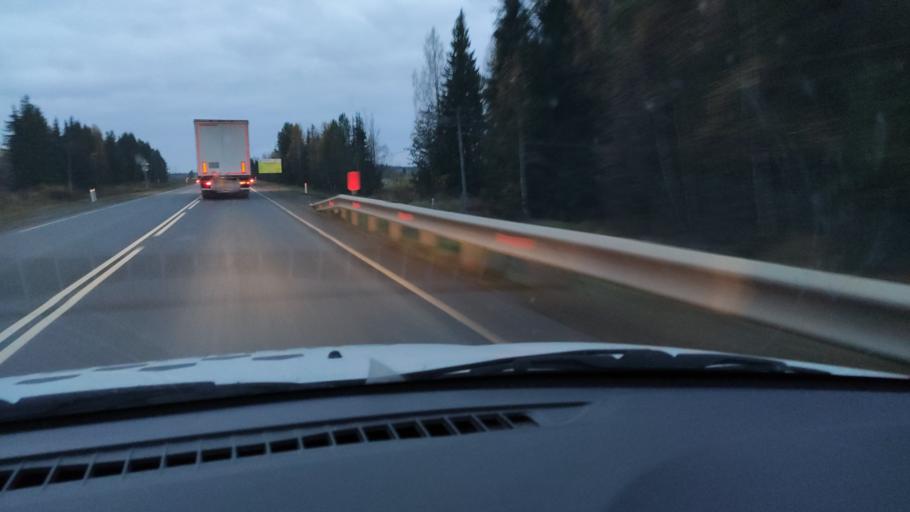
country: RU
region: Kirov
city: Kostino
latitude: 58.8371
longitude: 53.3042
